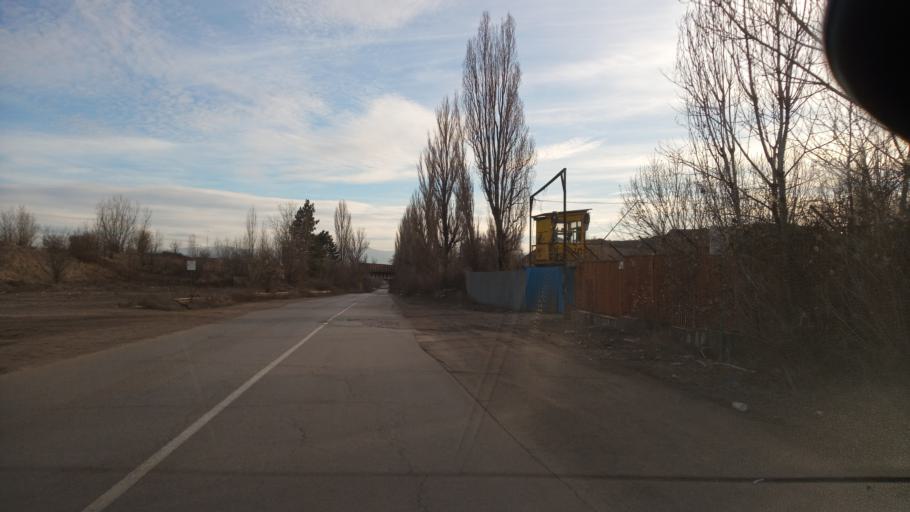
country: BG
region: Sofia-Capital
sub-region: Stolichna Obshtina
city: Bukhovo
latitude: 42.7368
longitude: 23.5541
